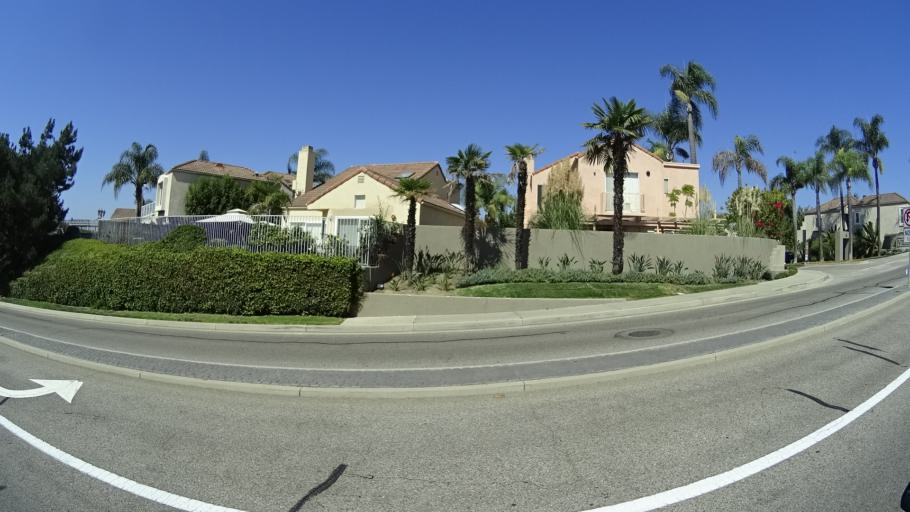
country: US
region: California
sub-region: Orange County
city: San Clemente
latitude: 33.4456
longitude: -117.5960
